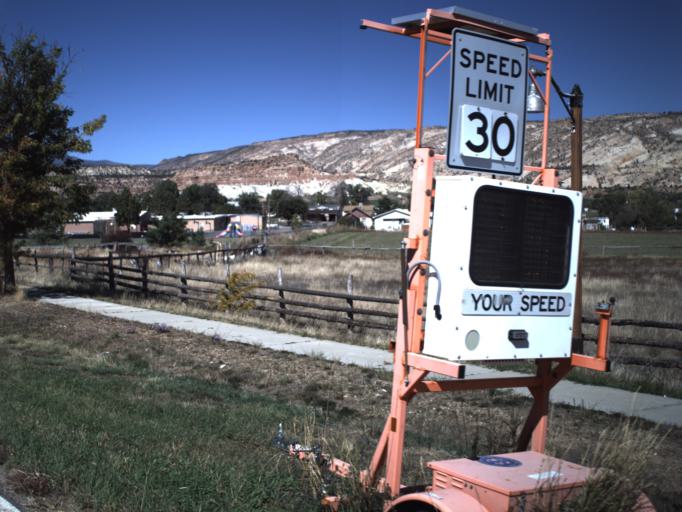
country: US
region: Utah
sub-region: Wayne County
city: Loa
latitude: 37.7681
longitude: -111.5930
